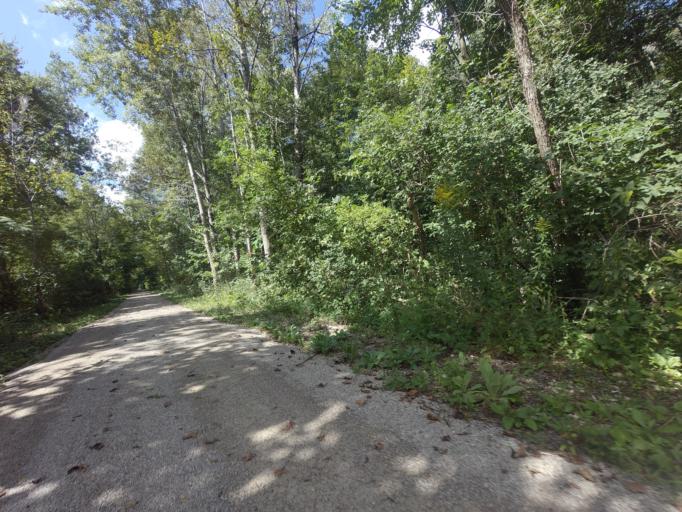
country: CA
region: Ontario
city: Huron East
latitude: 43.6760
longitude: -81.2892
